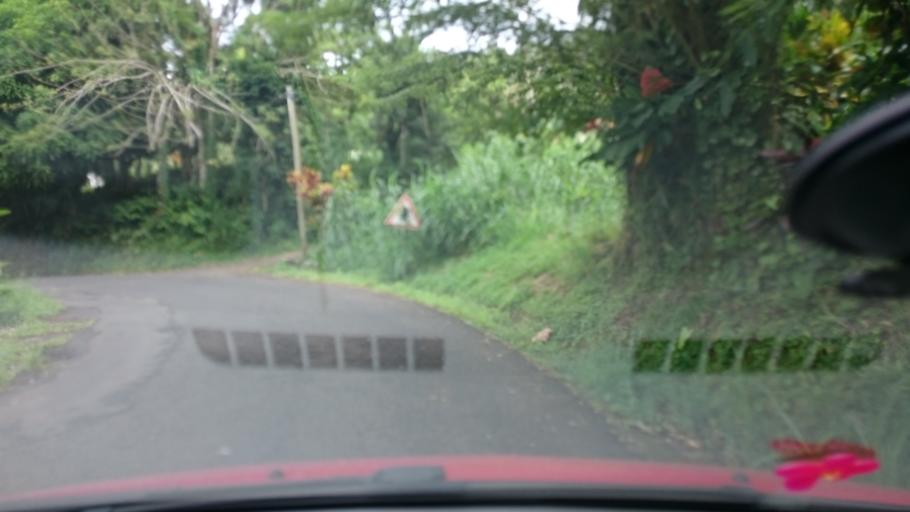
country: MQ
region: Martinique
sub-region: Martinique
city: Riviere-Pilote
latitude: 14.4962
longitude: -60.9226
